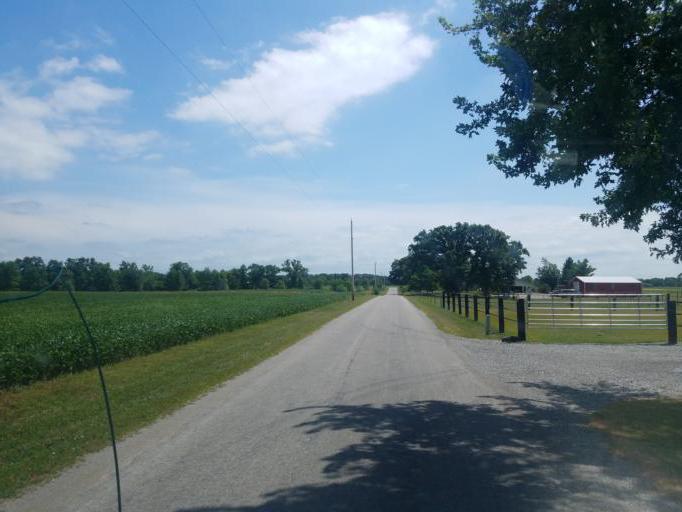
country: US
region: Indiana
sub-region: Allen County
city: Woodburn
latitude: 41.1719
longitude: -84.8693
